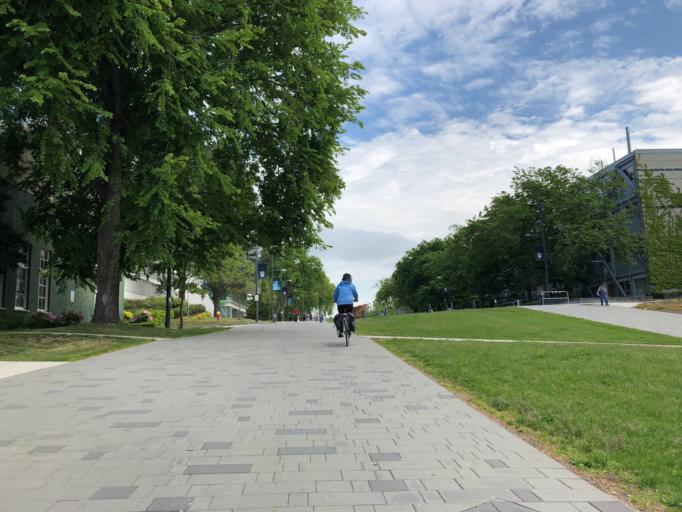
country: CA
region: British Columbia
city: West End
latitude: 49.2642
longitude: -123.2546
